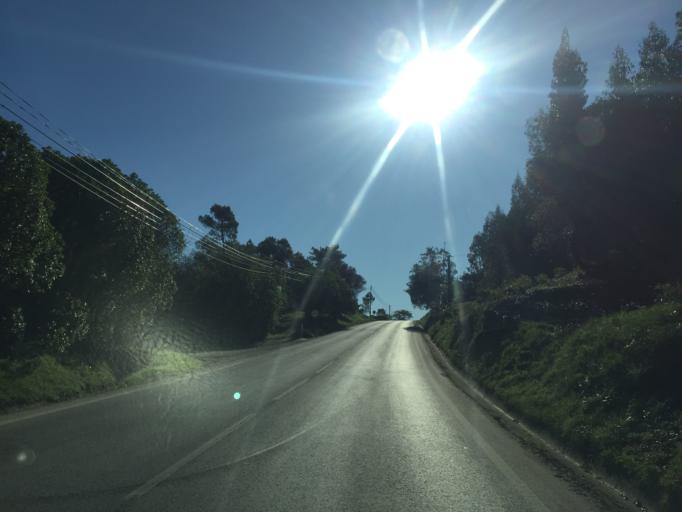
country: PT
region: Lisbon
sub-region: Sintra
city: Almargem
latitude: 38.8073
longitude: -9.2884
